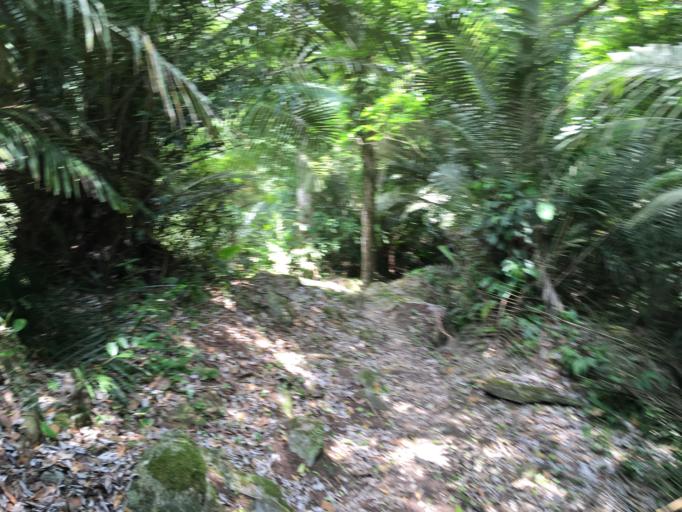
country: TW
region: Taiwan
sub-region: Yilan
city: Yilan
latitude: 24.4287
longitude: 121.6937
